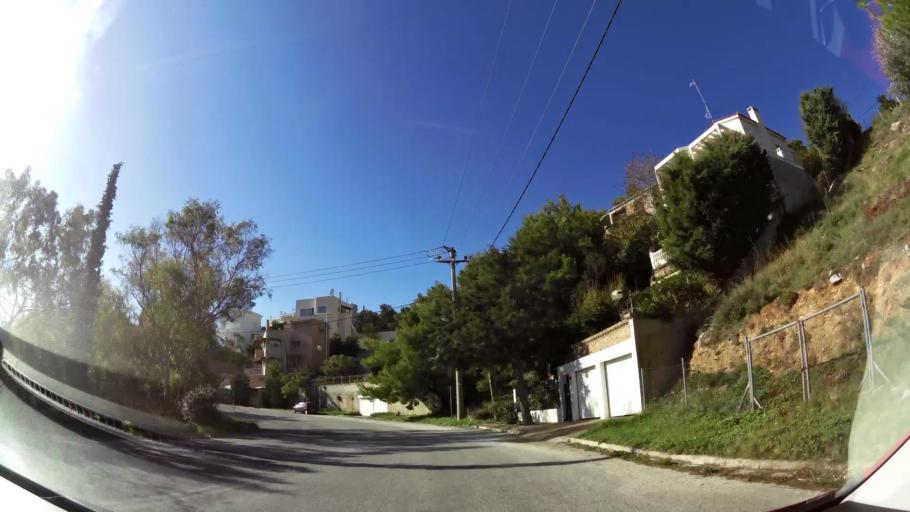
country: GR
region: Attica
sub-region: Nomarchia Anatolikis Attikis
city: Dhrafi
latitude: 38.0305
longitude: 23.8953
